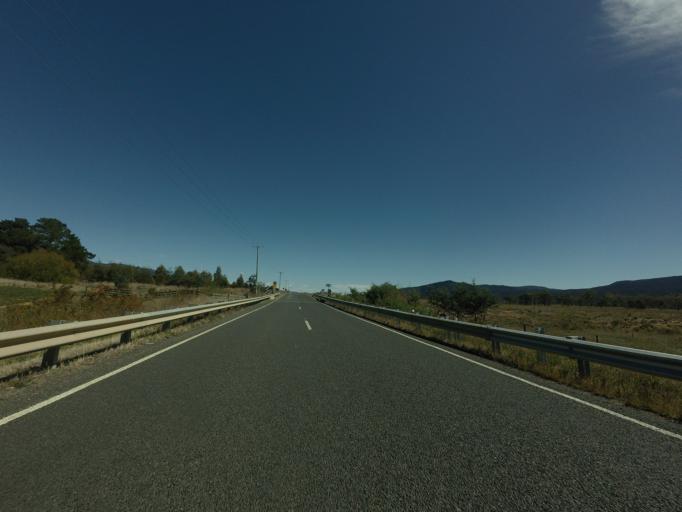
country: AU
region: Tasmania
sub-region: Break O'Day
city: St Helens
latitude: -41.7102
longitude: 147.8425
